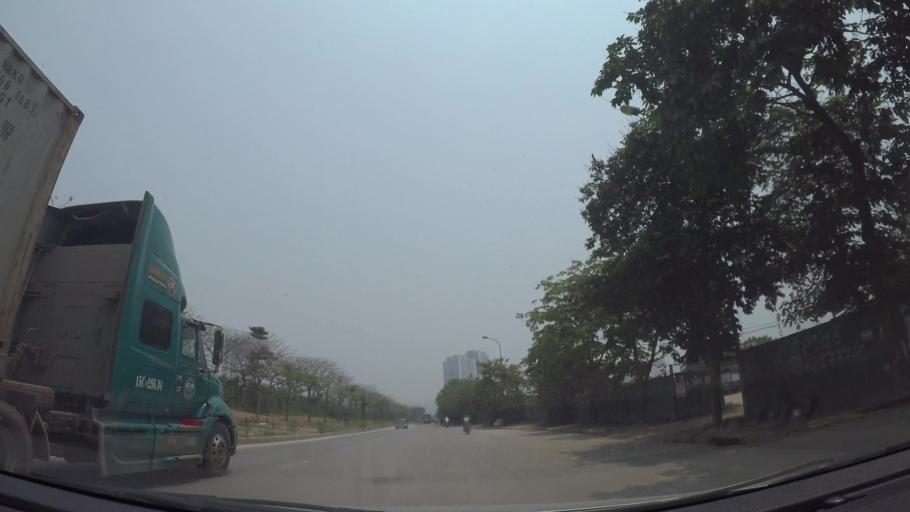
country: VN
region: Ha Noi
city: Thanh Xuan
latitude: 21.0032
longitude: 105.7751
